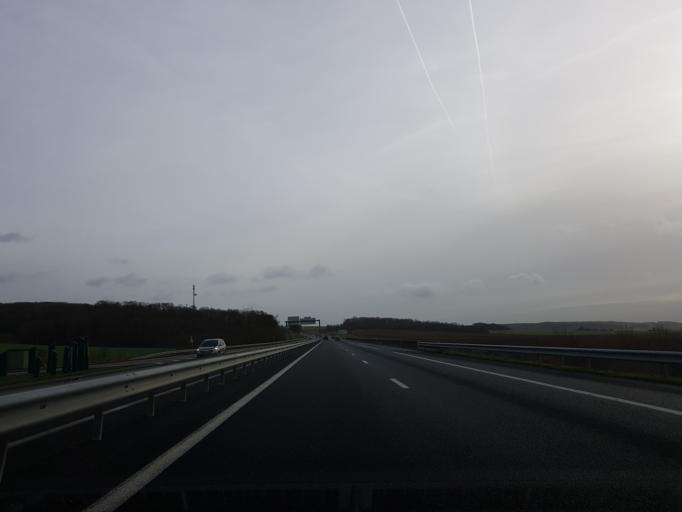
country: FR
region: Bourgogne
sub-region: Departement de l'Yonne
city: Soucy
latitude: 48.2653
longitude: 3.3027
